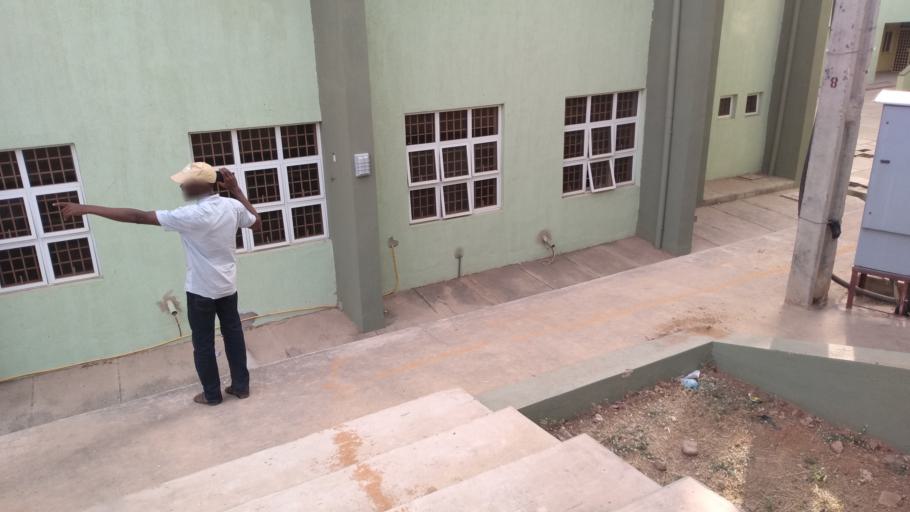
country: NG
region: Gombe
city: Gombe
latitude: 10.3051
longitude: 11.1758
